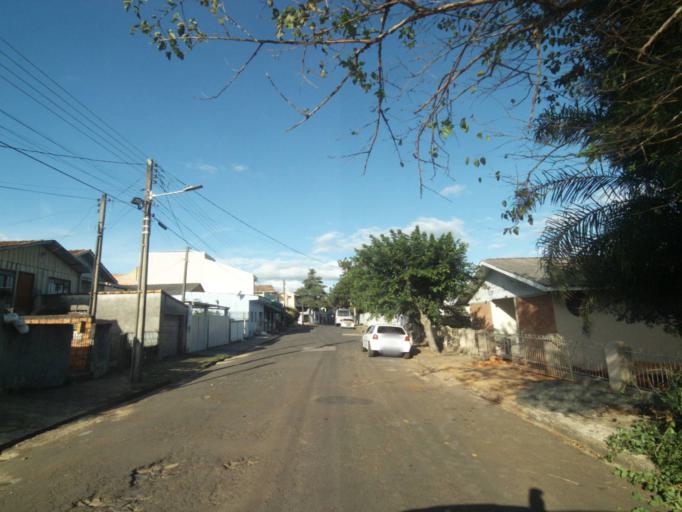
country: BR
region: Parana
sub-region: Telemaco Borba
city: Telemaco Borba
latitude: -24.3336
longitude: -50.6169
